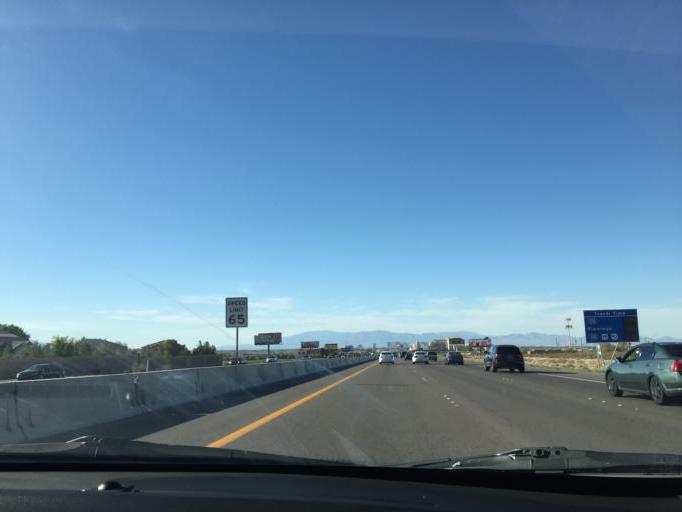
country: US
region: Nevada
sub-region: Clark County
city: Enterprise
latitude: 35.9759
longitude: -115.1812
